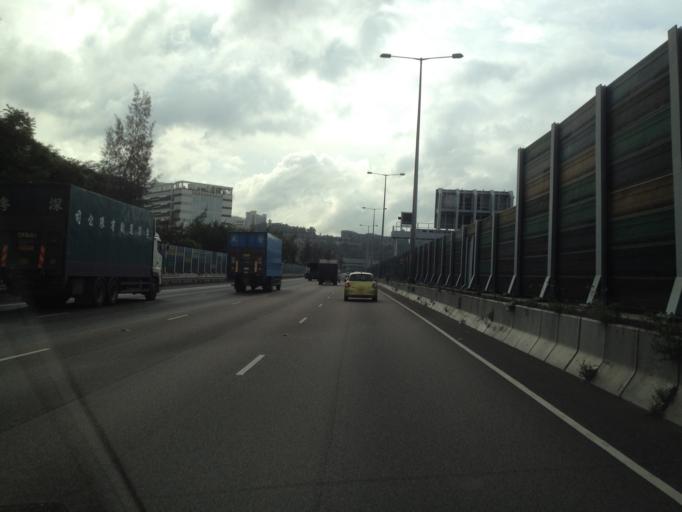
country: HK
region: Tai Po
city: Tai Po
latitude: 22.4264
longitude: 114.2078
